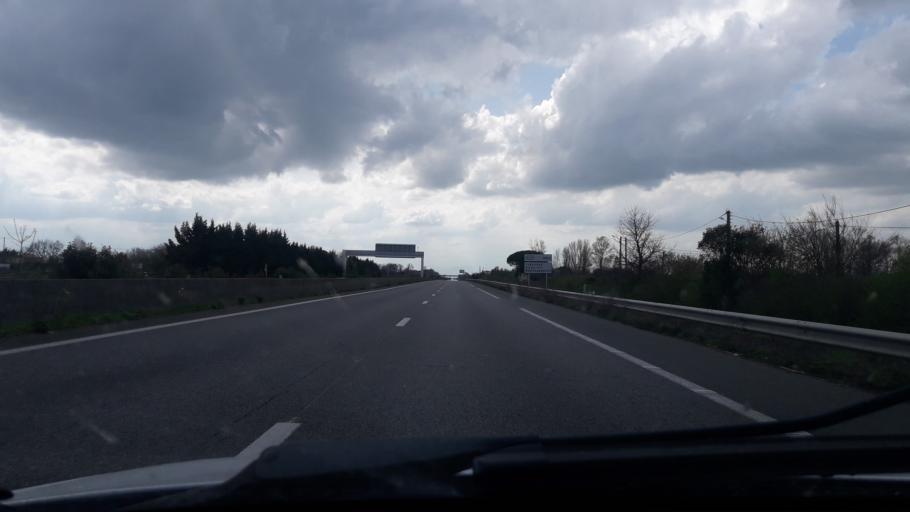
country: FR
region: Midi-Pyrenees
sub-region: Departement de la Haute-Garonne
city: Marquefave
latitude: 43.3268
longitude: 1.2293
